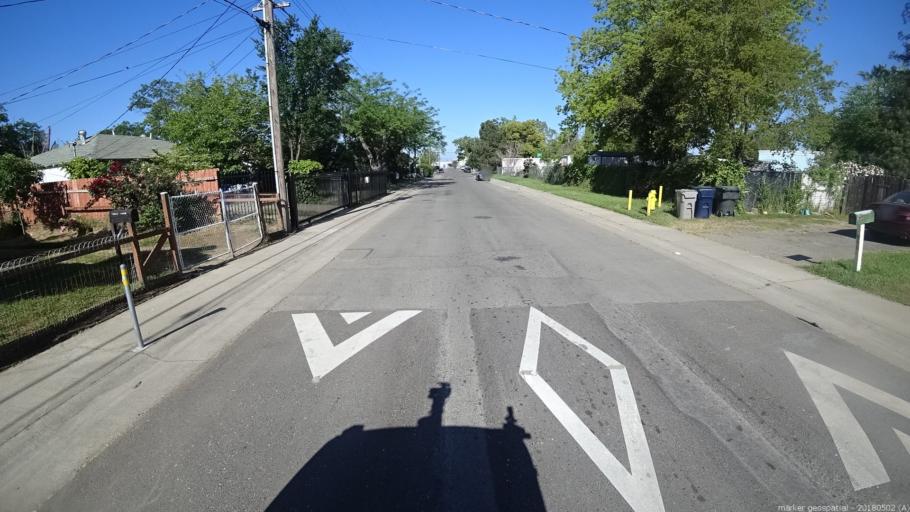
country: US
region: California
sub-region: Sacramento County
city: Arden-Arcade
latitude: 38.6184
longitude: -121.4242
